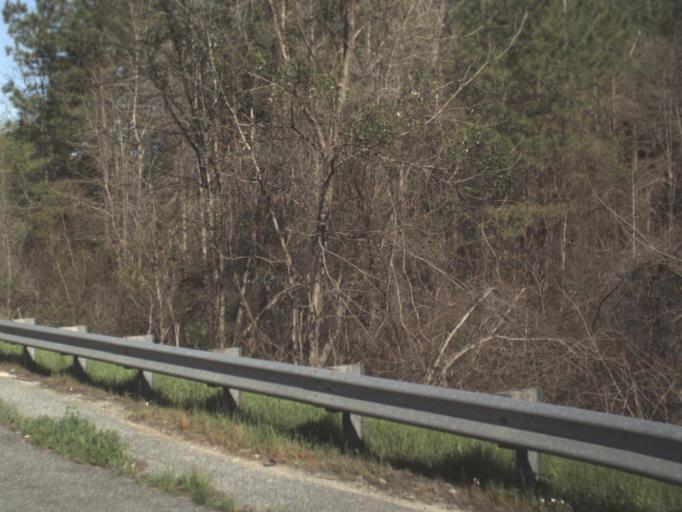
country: US
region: Florida
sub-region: Jackson County
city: Malone
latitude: 30.9762
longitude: -85.0185
